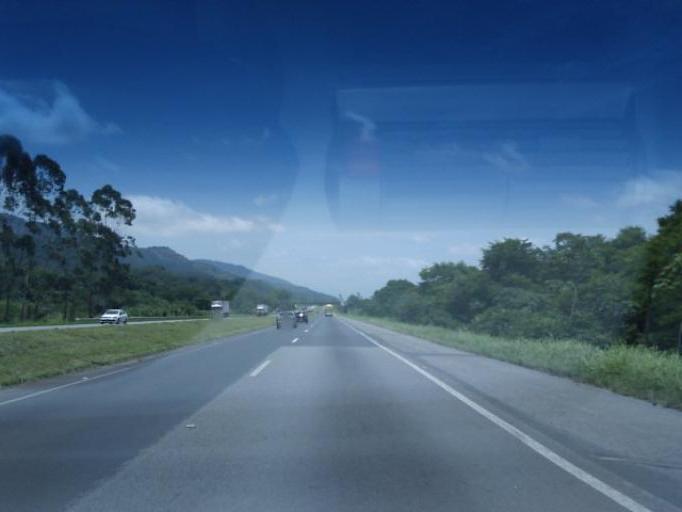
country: BR
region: Sao Paulo
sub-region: Miracatu
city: Miracatu
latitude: -24.2743
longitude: -47.4106
